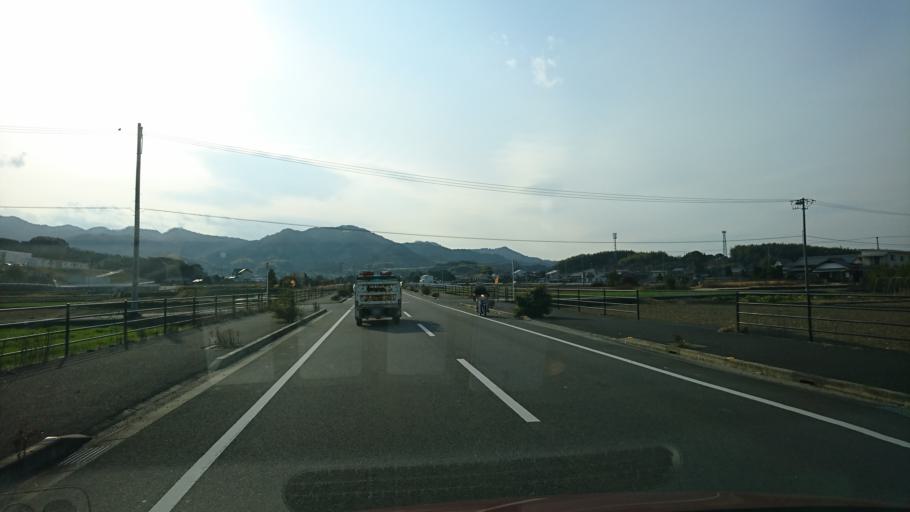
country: JP
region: Ehime
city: Saijo
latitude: 34.0247
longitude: 133.0001
